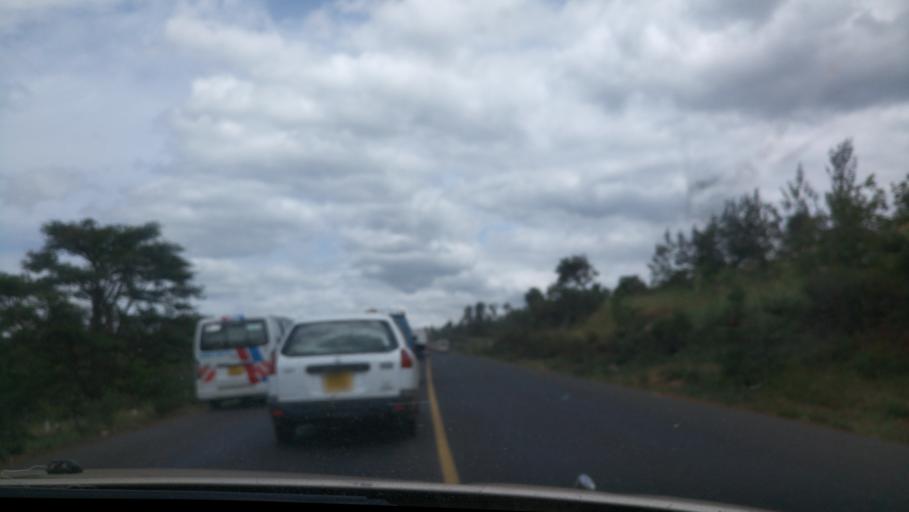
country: KE
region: Murang'a District
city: Maragua
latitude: -0.8516
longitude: 37.2333
